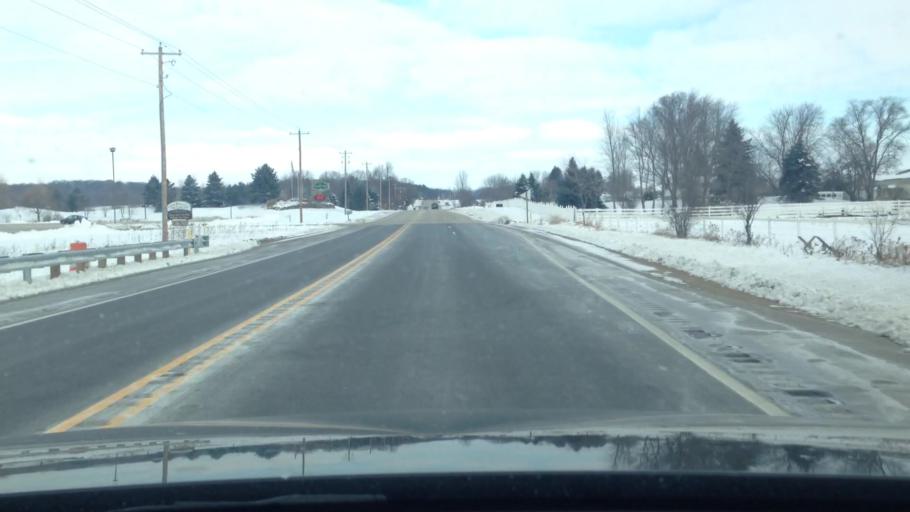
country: US
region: Wisconsin
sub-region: Walworth County
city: Lake Geneva
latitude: 42.6203
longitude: -88.4138
